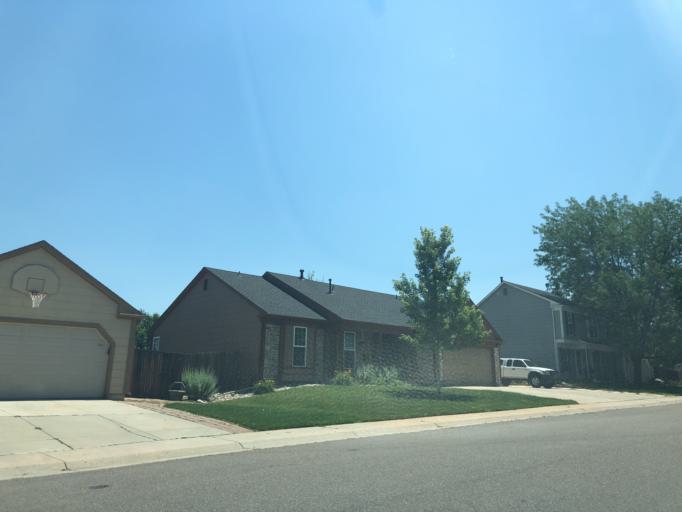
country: US
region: Colorado
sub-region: Arapahoe County
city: Dove Valley
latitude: 39.6194
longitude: -104.7557
